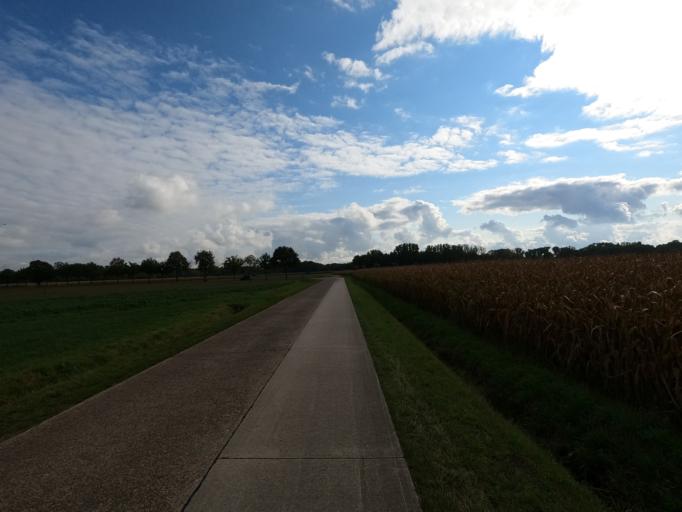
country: BE
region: Flanders
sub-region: Provincie Antwerpen
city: Kasterlee
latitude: 51.2208
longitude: 4.9582
